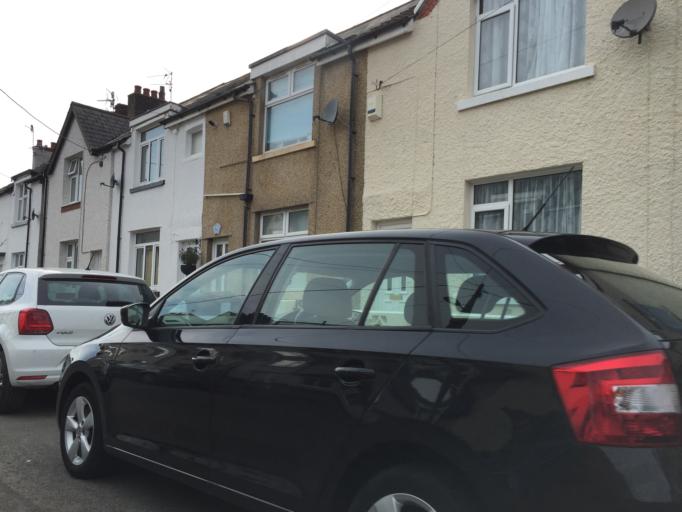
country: GB
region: Wales
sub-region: Caerphilly County Borough
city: Caerphilly
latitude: 51.5881
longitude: -3.2213
